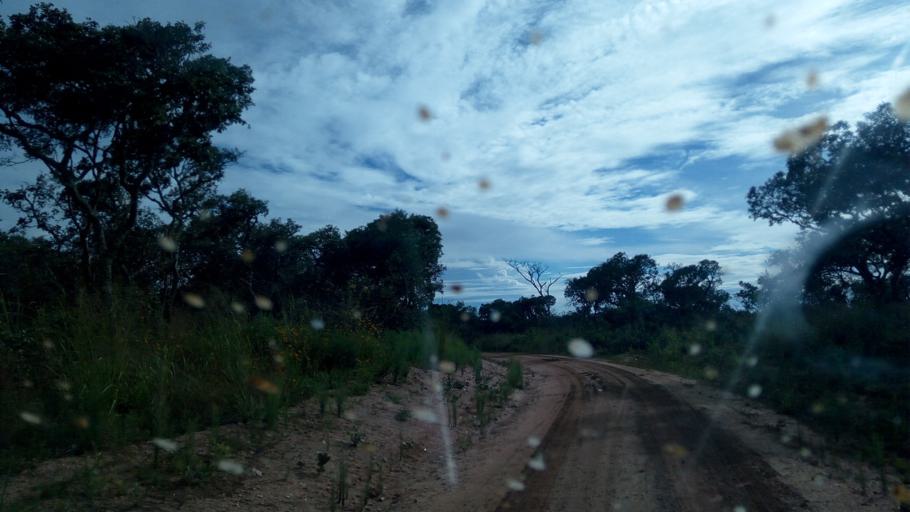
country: CD
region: Katanga
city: Kalemie
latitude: -6.3296
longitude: 29.0183
